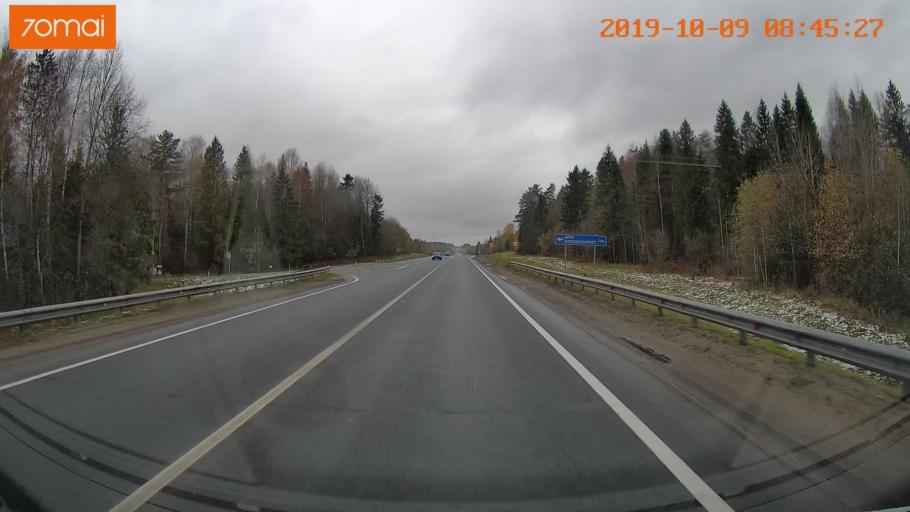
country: RU
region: Vologda
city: Gryazovets
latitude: 59.0482
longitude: 40.0898
